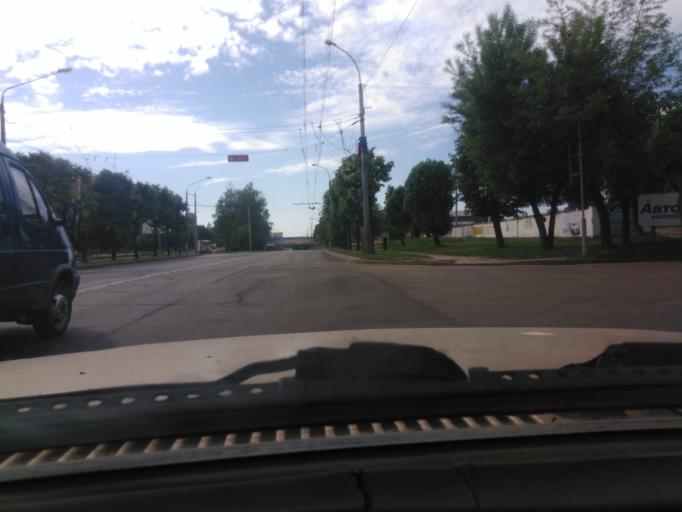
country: BY
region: Mogilev
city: Buynichy
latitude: 53.8947
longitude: 30.2971
